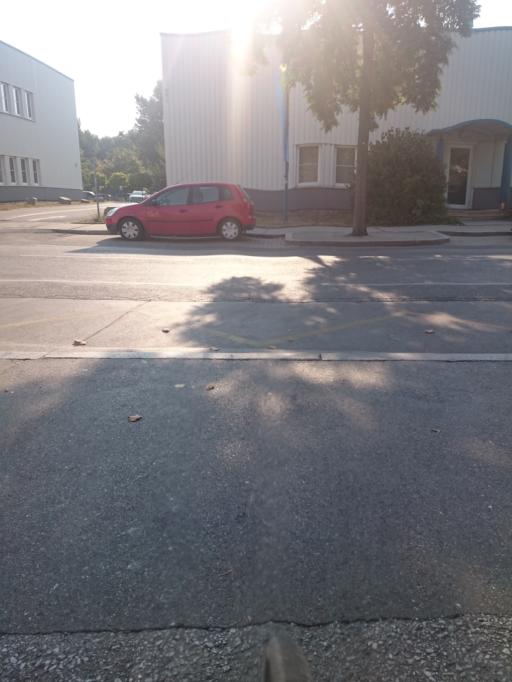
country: AT
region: Lower Austria
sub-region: Politischer Bezirk Korneuburg
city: Langenzersdorf
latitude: 48.2685
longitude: 16.4002
